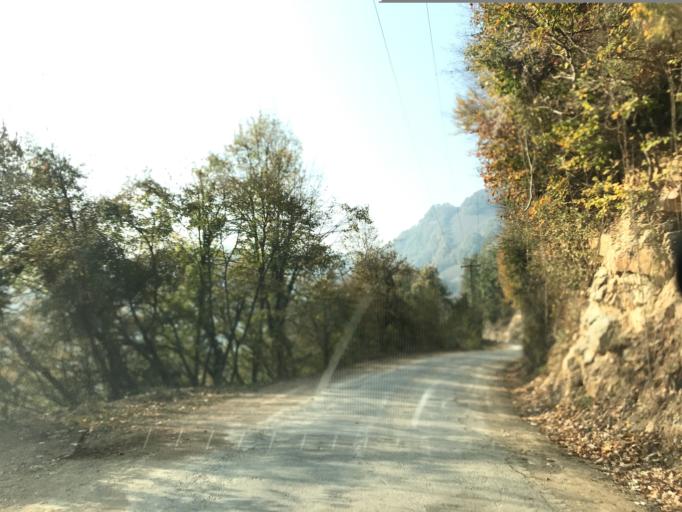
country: TR
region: Duzce
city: Cumayeri
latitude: 40.9384
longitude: 30.9318
